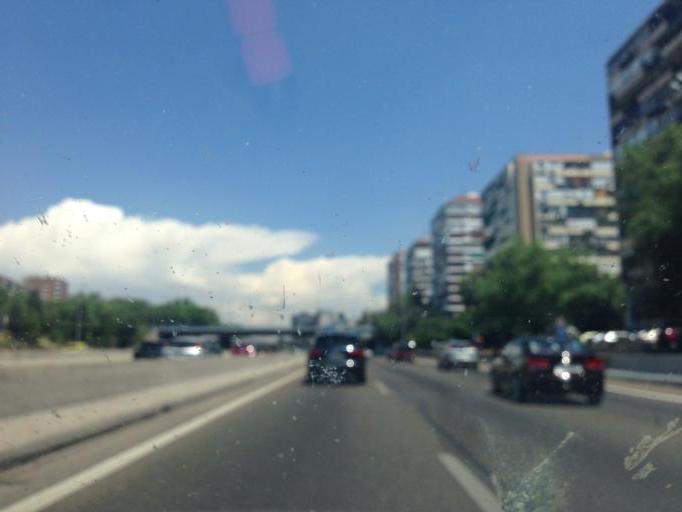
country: ES
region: Madrid
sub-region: Provincia de Madrid
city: Moratalaz
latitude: 40.4326
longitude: -3.6604
